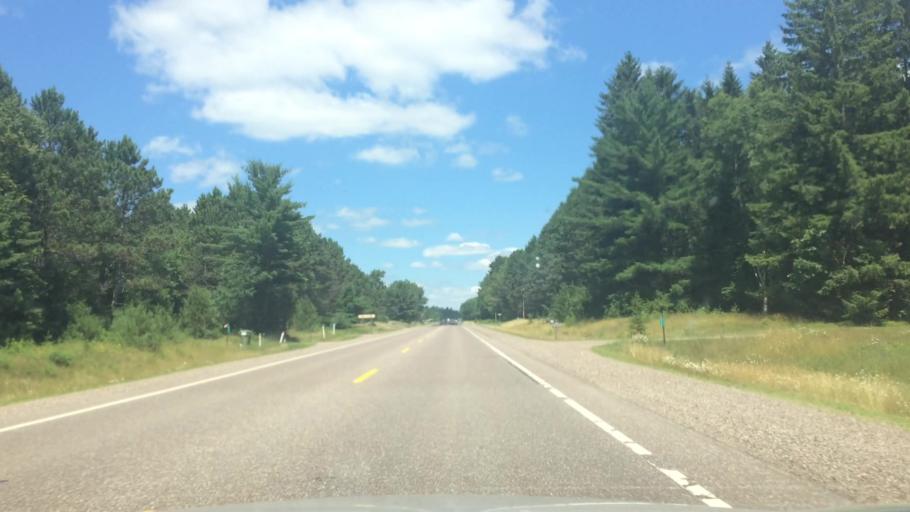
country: US
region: Wisconsin
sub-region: Vilas County
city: Lac du Flambeau
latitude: 45.9718
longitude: -89.6996
